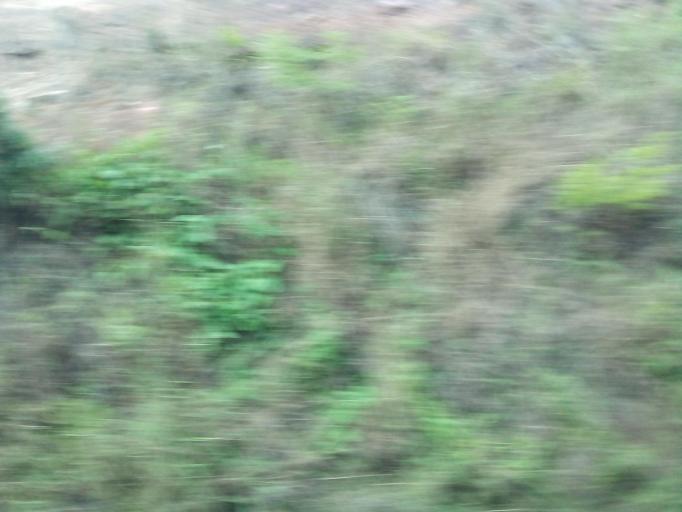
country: BR
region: Minas Gerais
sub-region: Caete
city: Caete
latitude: -19.8987
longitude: -43.7262
